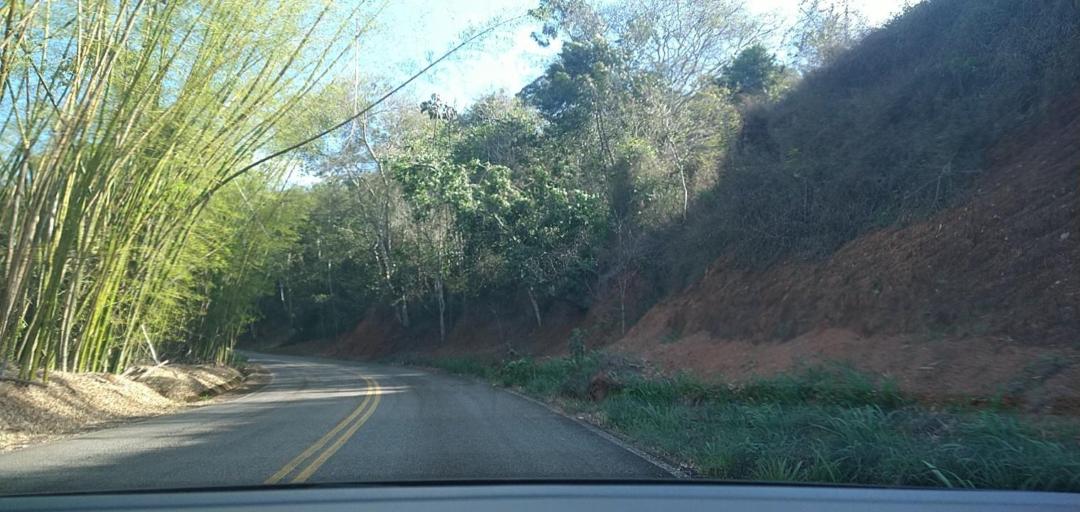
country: BR
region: Minas Gerais
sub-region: Alvinopolis
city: Alvinopolis
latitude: -20.1700
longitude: -42.9214
